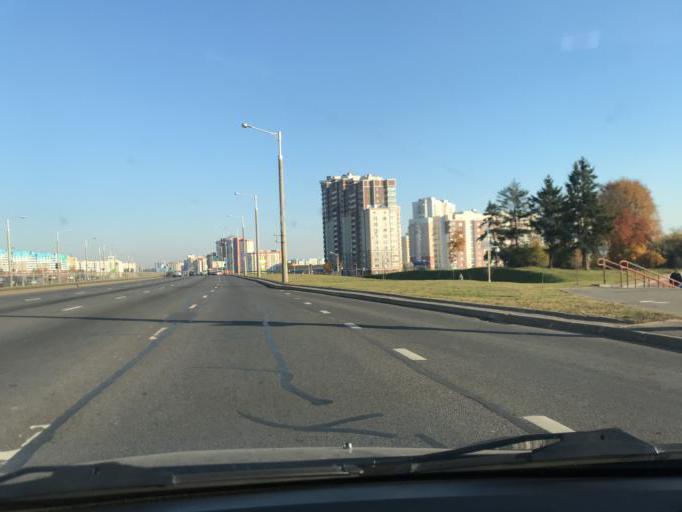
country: BY
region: Minsk
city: Novoye Medvezhino
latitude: 53.9075
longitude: 27.4258
